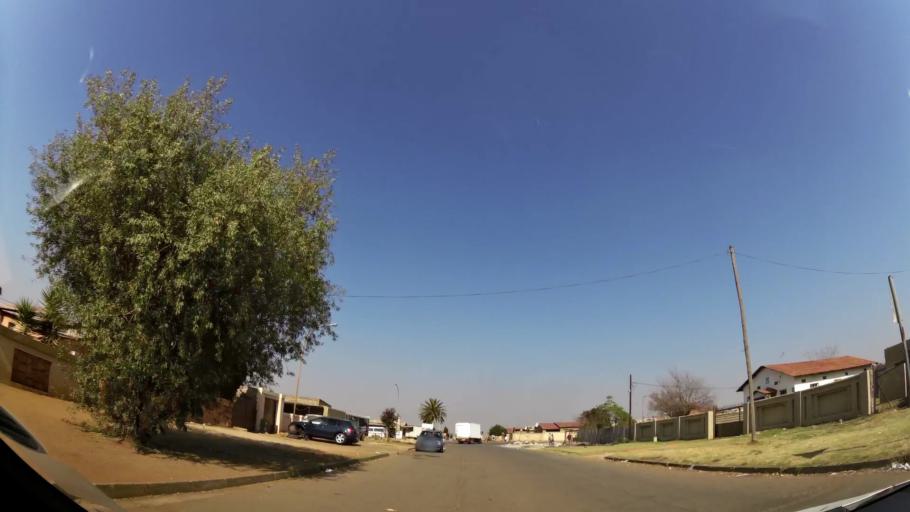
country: ZA
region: Gauteng
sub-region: Ekurhuleni Metropolitan Municipality
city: Benoni
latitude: -26.2227
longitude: 28.3028
